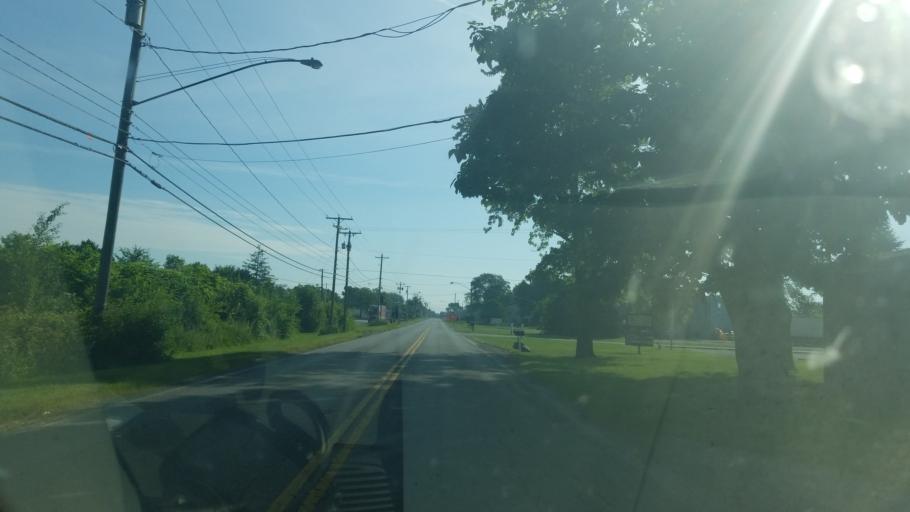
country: US
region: Ohio
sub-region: Hancock County
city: Findlay
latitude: 41.0176
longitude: -83.6760
